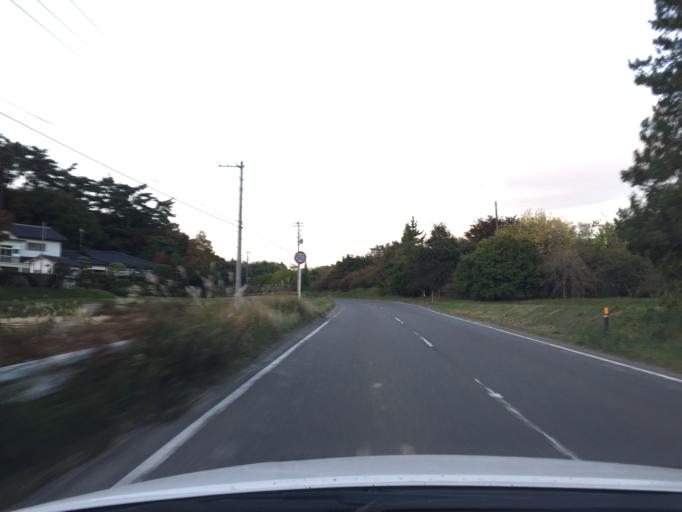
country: JP
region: Fukushima
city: Koriyama
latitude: 37.3549
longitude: 140.4471
